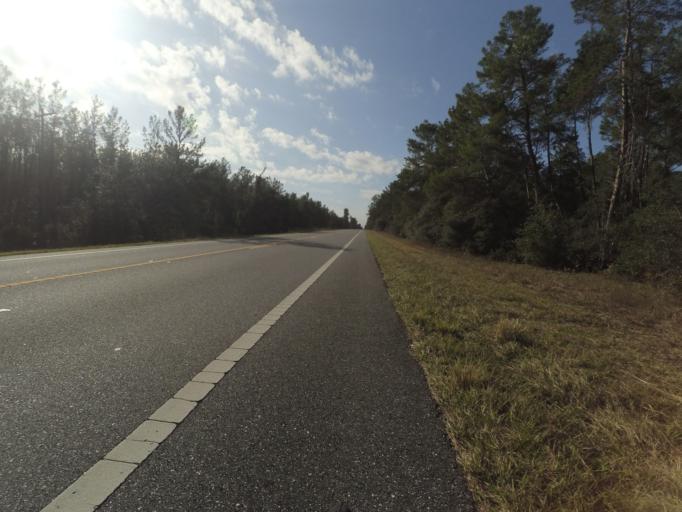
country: US
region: Florida
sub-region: Lake County
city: Astor
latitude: 29.0861
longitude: -81.6251
